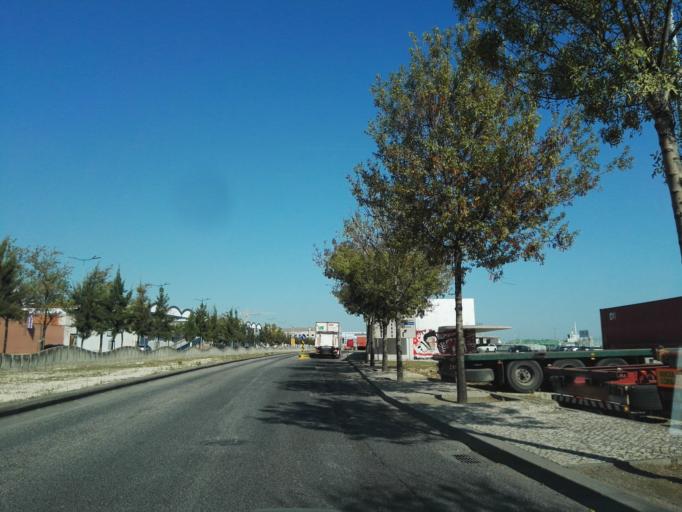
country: PT
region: Lisbon
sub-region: Lisbon
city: Lisbon
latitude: 38.7376
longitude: -9.1026
